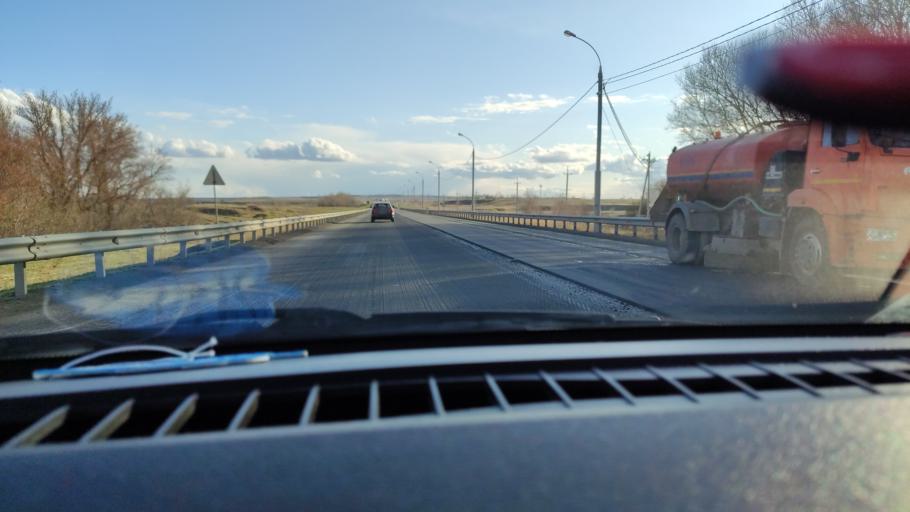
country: RU
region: Saratov
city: Yelshanka
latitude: 51.8197
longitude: 46.2147
